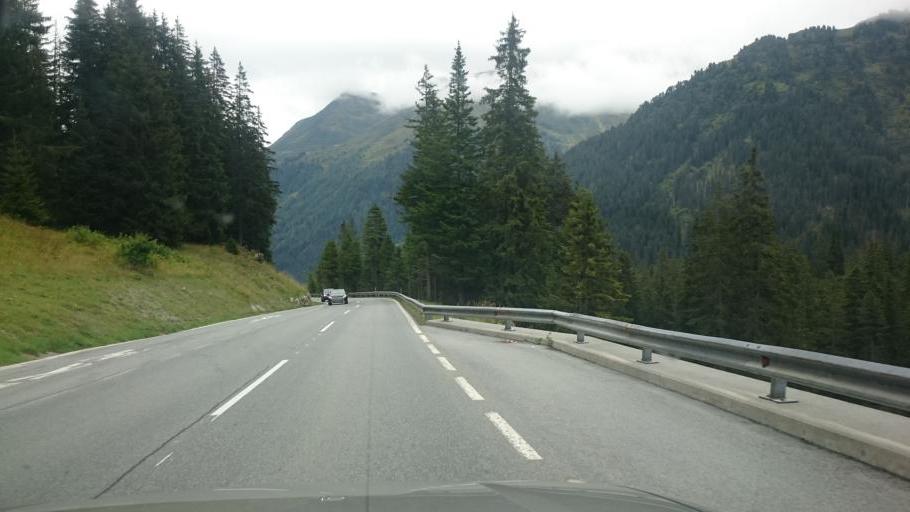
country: AT
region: Tyrol
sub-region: Politischer Bezirk Landeck
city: Sankt Anton am Arlberg
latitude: 47.1186
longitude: 10.2290
